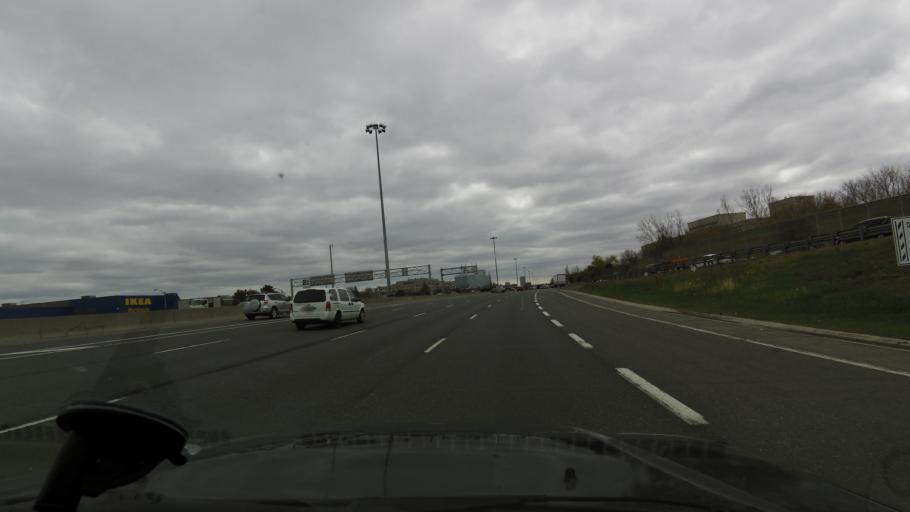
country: CA
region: Ontario
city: Willowdale
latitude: 43.8092
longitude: -79.3470
